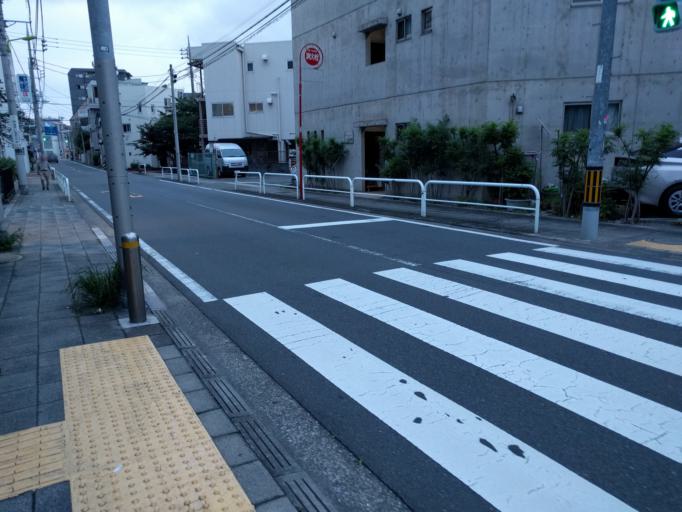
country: JP
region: Tokyo
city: Tokyo
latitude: 35.6372
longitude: 139.6820
